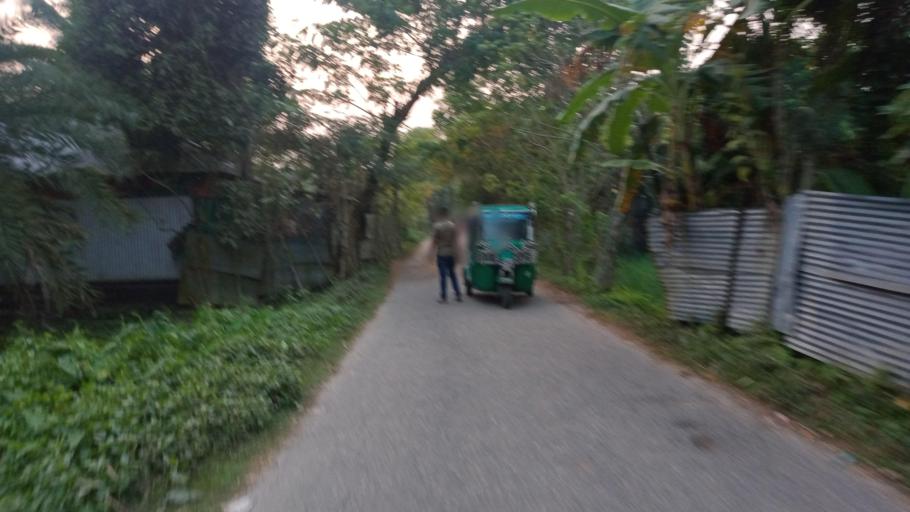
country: BD
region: Chittagong
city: Hajiganj
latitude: 23.3675
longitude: 90.9858
